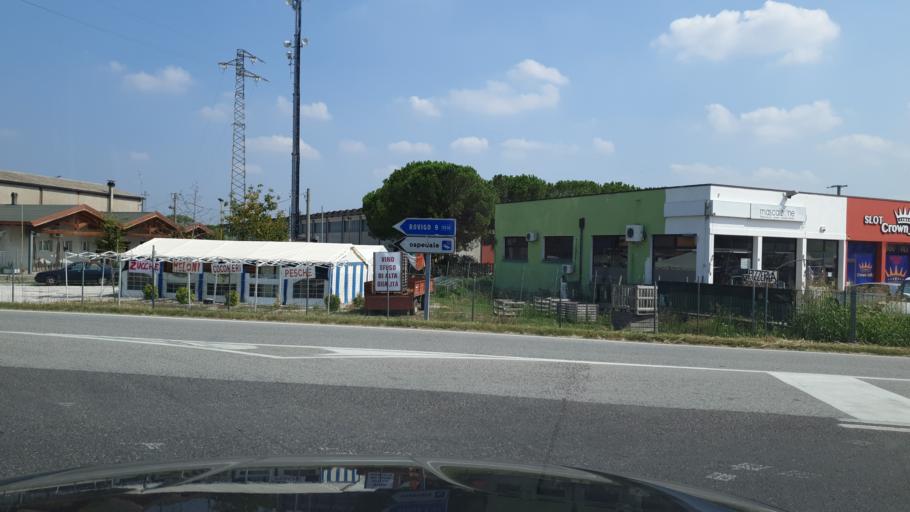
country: IT
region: Veneto
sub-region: Provincia di Rovigo
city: Bosaro
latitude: 45.0071
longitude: 11.7647
